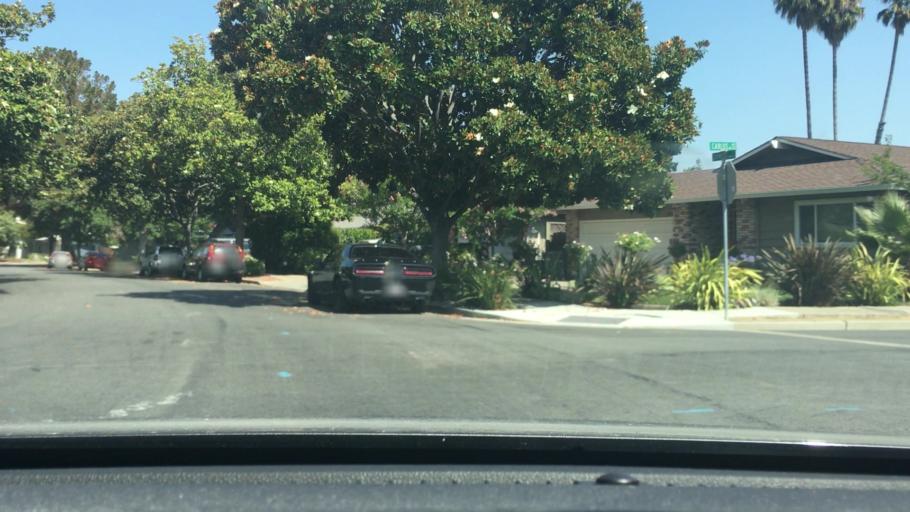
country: US
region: California
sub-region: San Mateo County
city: Atherton
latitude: 37.4693
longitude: -122.2180
